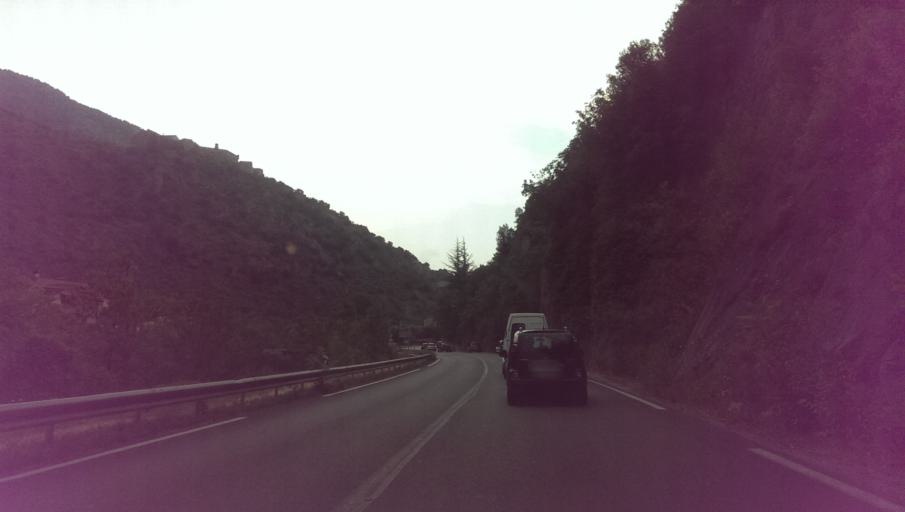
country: FR
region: Languedoc-Roussillon
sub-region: Departement des Pyrenees-Orientales
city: Vernet-les-Bains
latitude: 42.5844
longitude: 2.3627
